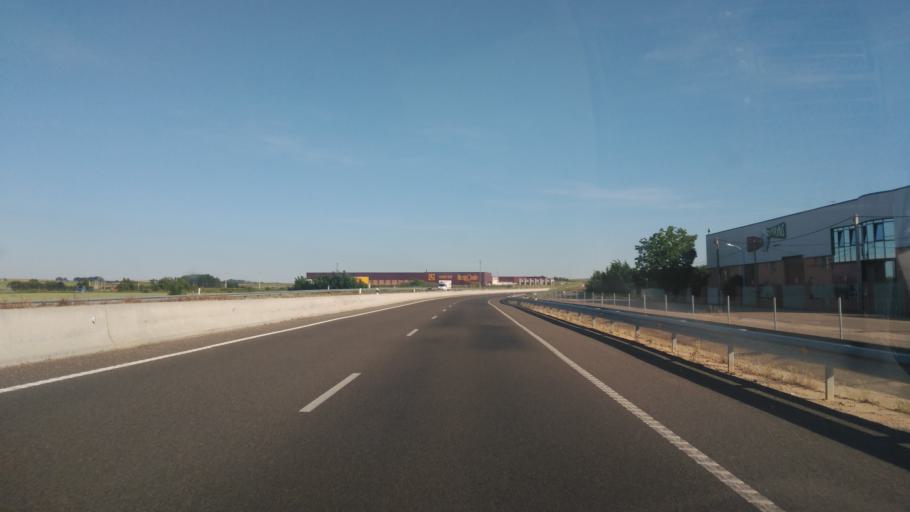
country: ES
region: Castille and Leon
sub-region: Provincia de Zamora
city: Morales del Vino
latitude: 41.4665
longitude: -5.7356
